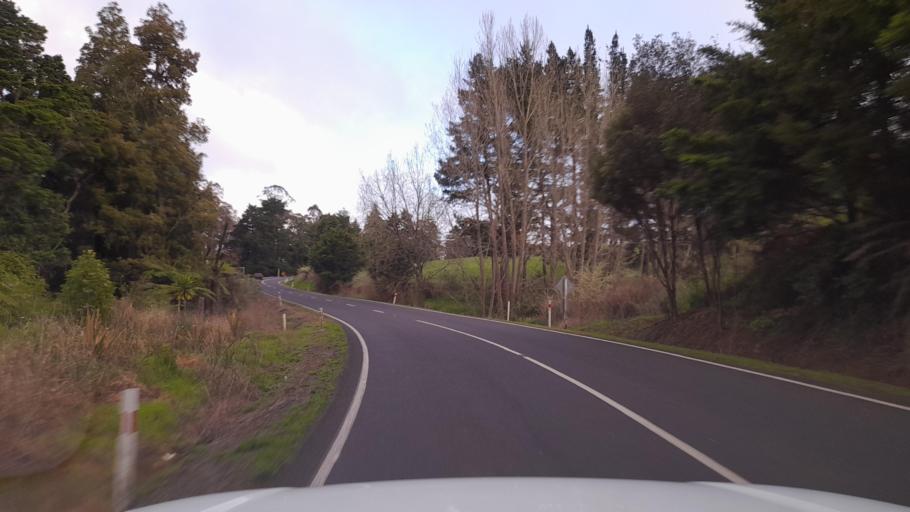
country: NZ
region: Northland
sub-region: Far North District
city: Waimate North
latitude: -35.5173
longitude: 173.8324
